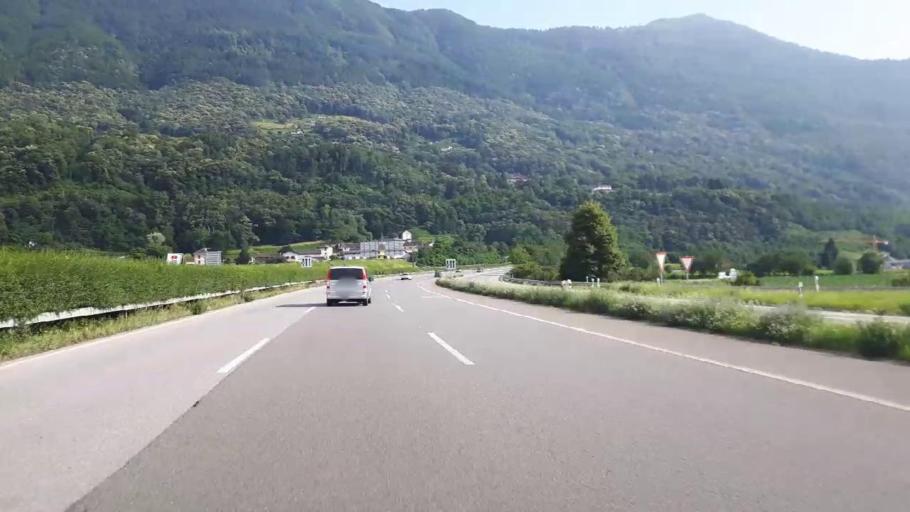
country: CH
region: Ticino
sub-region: Bellinzona District
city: Camorino
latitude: 46.1622
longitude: 8.9909
